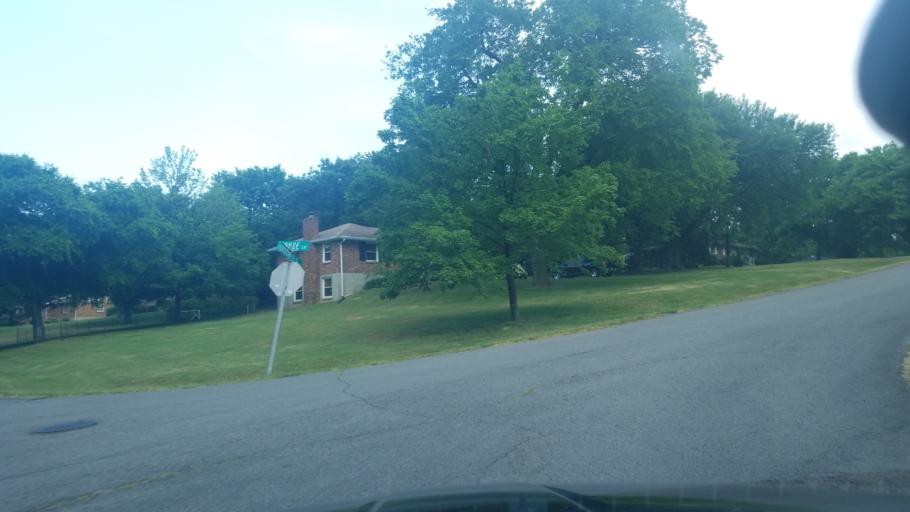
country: US
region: Tennessee
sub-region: Davidson County
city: Nashville
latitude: 36.2334
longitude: -86.7409
